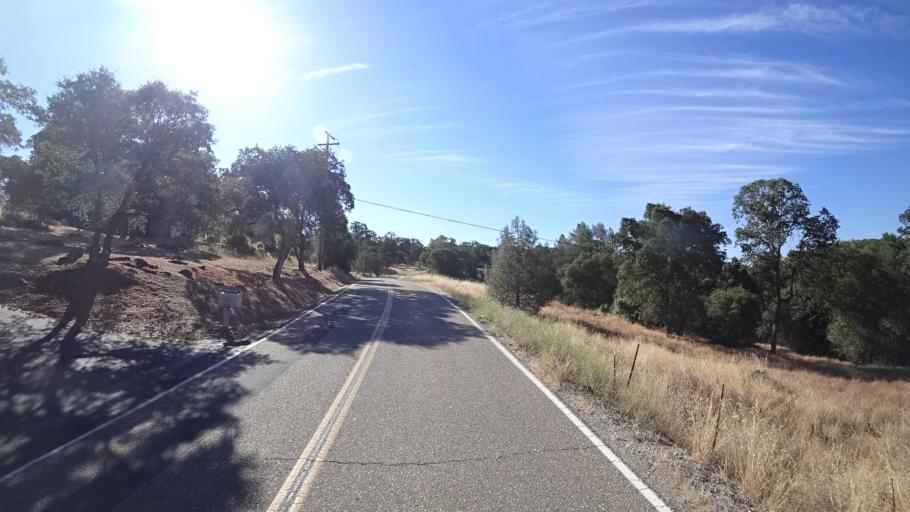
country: US
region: California
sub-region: Calaveras County
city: San Andreas
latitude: 38.1853
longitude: -120.6584
